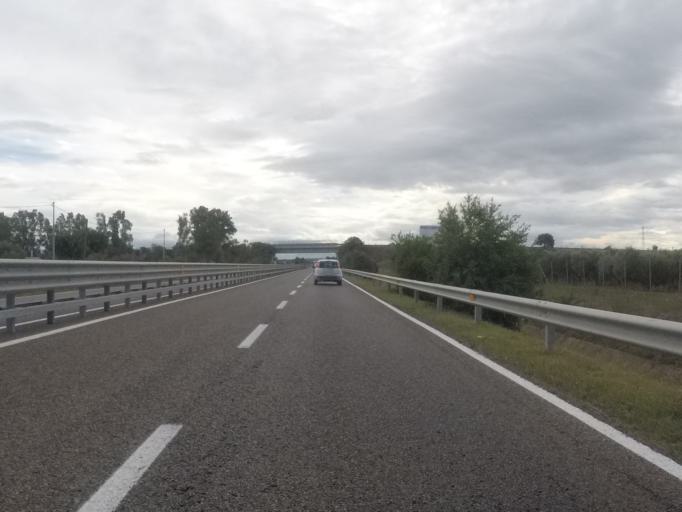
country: IT
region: Sardinia
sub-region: Provincia di Cagliari
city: Villaspeciosa
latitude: 39.3071
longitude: 8.9151
